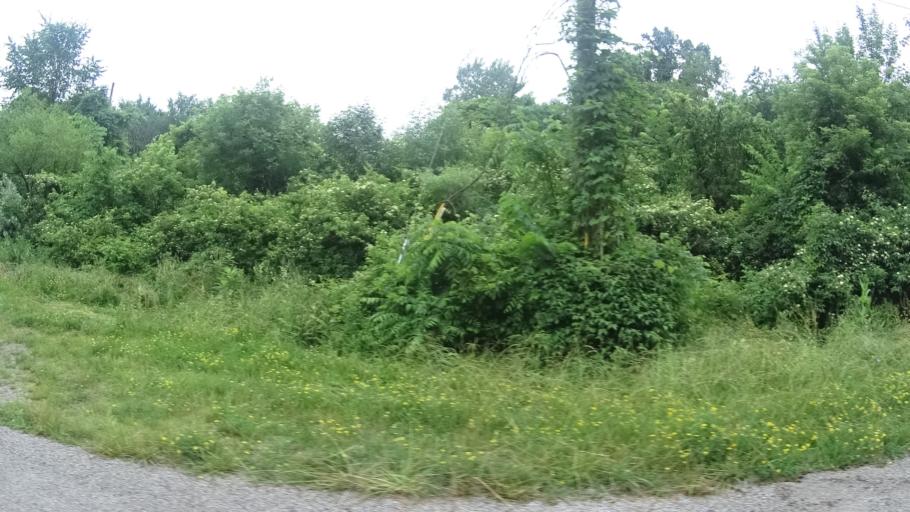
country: US
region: Ohio
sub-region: Erie County
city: Milan
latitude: 41.3357
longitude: -82.5746
